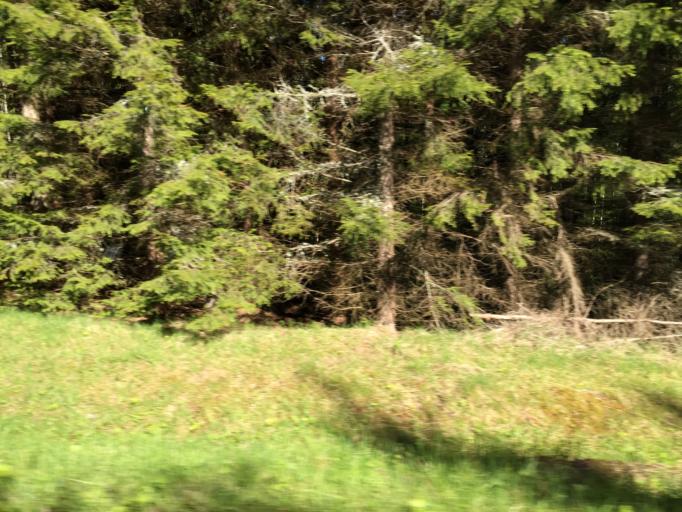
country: SE
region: Soedermanland
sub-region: Vingakers Kommun
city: Vingaker
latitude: 58.9621
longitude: 15.6736
